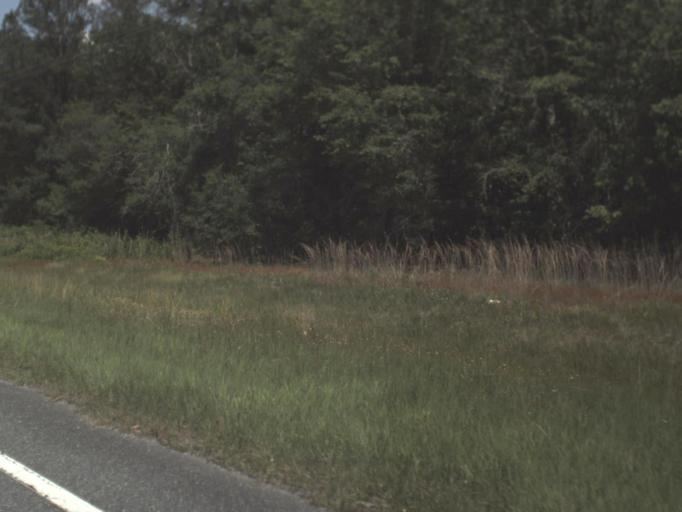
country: US
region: Florida
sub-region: Bradford County
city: Starke
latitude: 29.9670
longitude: -82.1976
